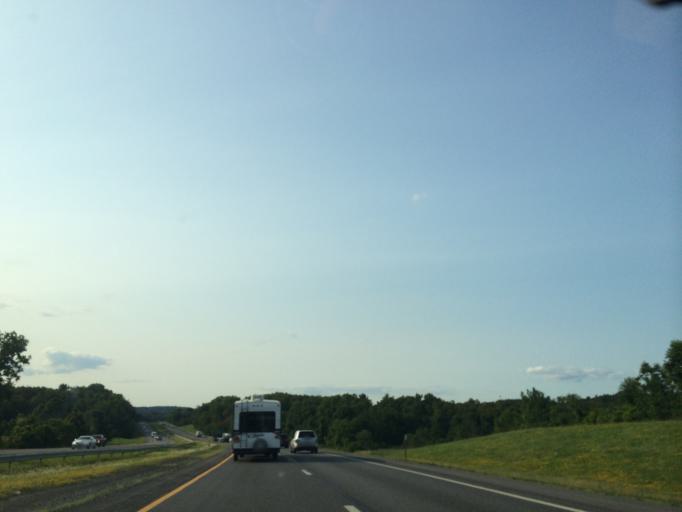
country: US
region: New York
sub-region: Albany County
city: Ravena
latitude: 42.4368
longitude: -73.8038
